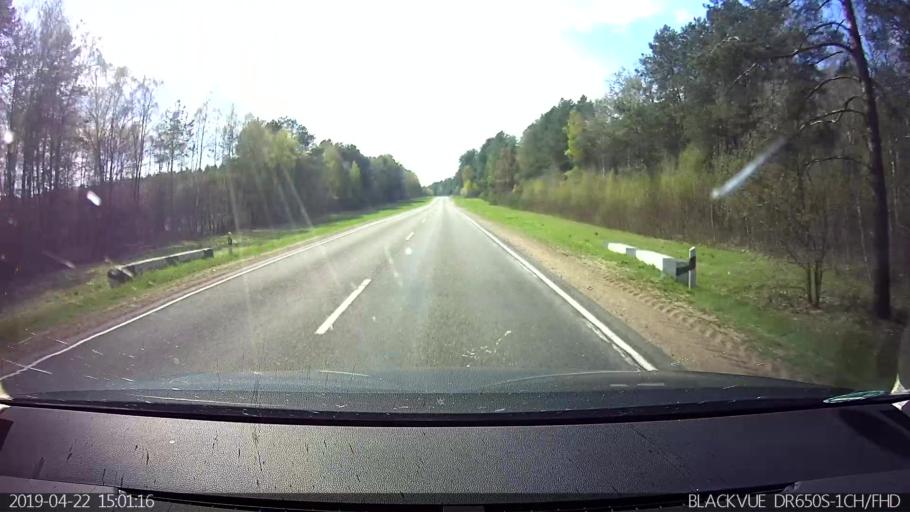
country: BY
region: Brest
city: Zhabinka
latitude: 52.3526
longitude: 23.9707
